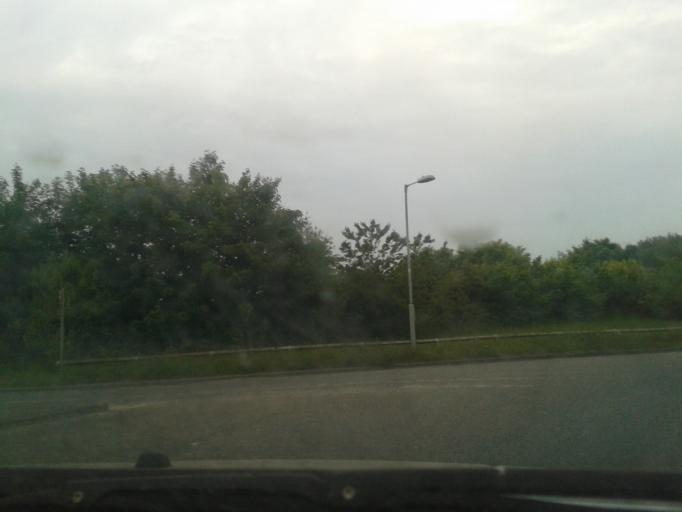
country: IE
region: Leinster
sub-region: Dublin City
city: Finglas
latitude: 53.4243
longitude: -6.3056
